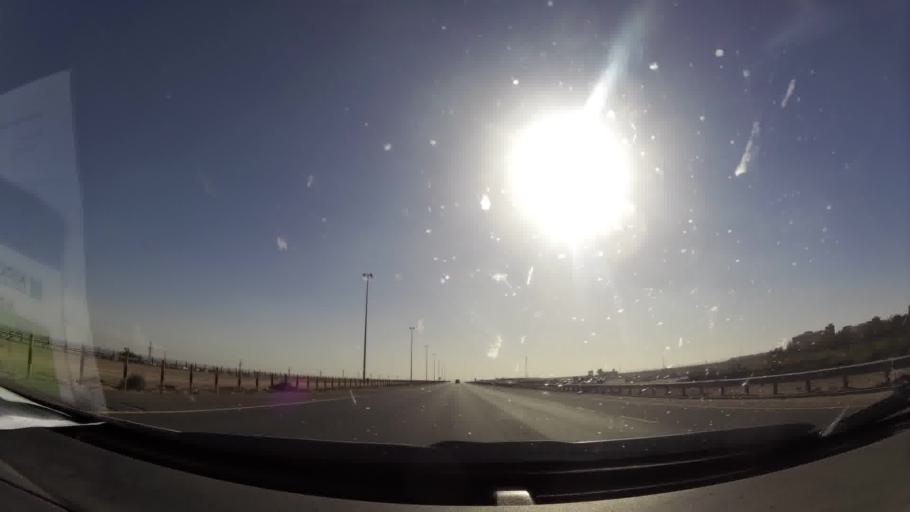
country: KW
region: Muhafazat al Jahra'
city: Al Jahra'
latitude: 29.4584
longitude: 47.7603
